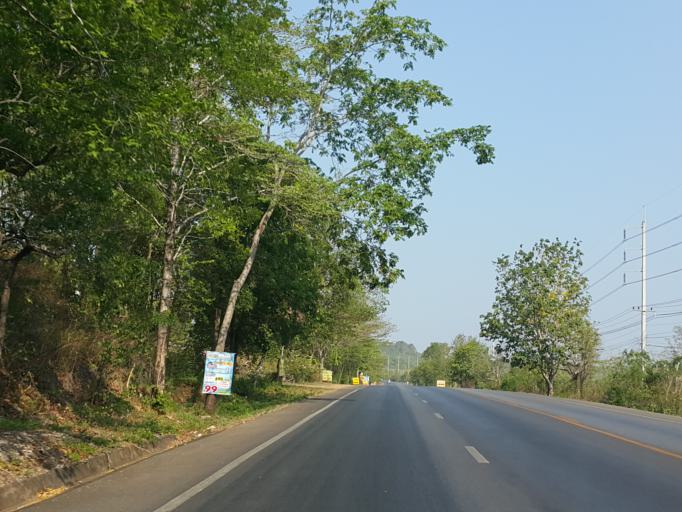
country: TH
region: Kanchanaburi
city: Sai Yok
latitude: 14.1103
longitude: 99.2107
